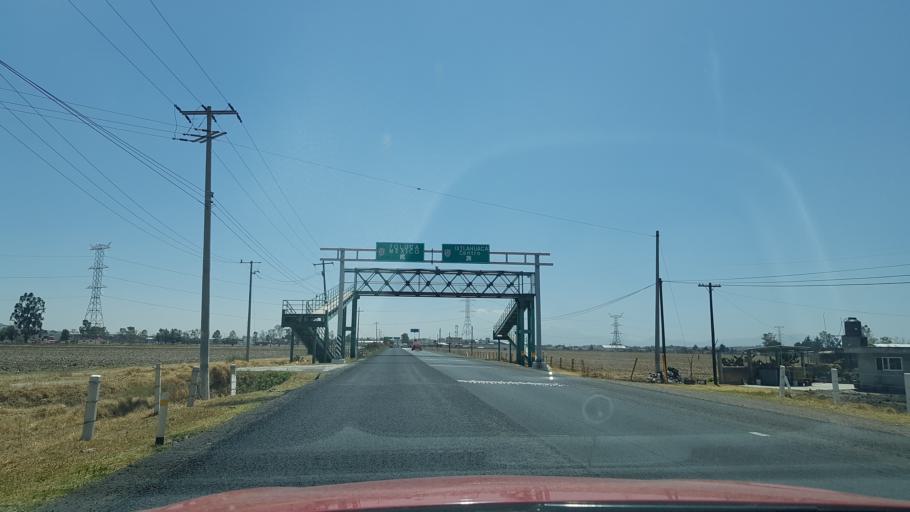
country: MX
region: Mexico
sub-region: Ixtlahuaca
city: Santo Domingo de Guzman
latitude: 19.5853
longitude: -99.7696
